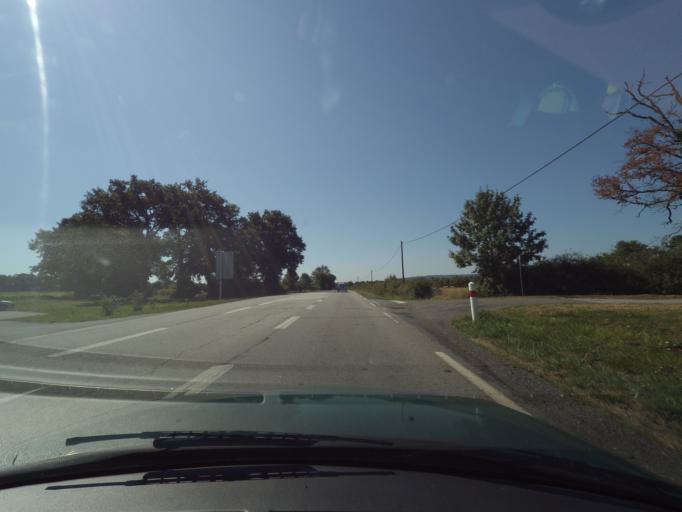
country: FR
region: Limousin
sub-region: Departement de la Haute-Vienne
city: Bellac
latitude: 46.1066
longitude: 1.0739
